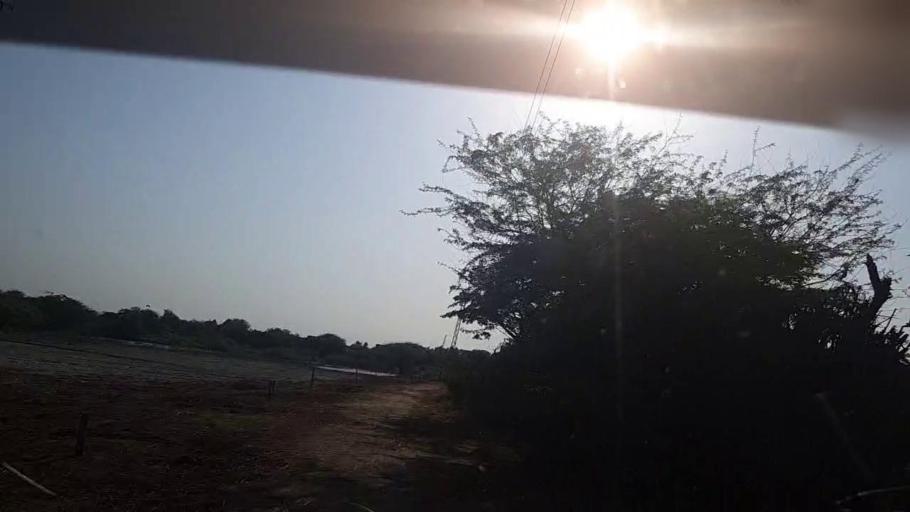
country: PK
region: Sindh
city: Talhar
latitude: 24.8549
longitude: 68.8516
